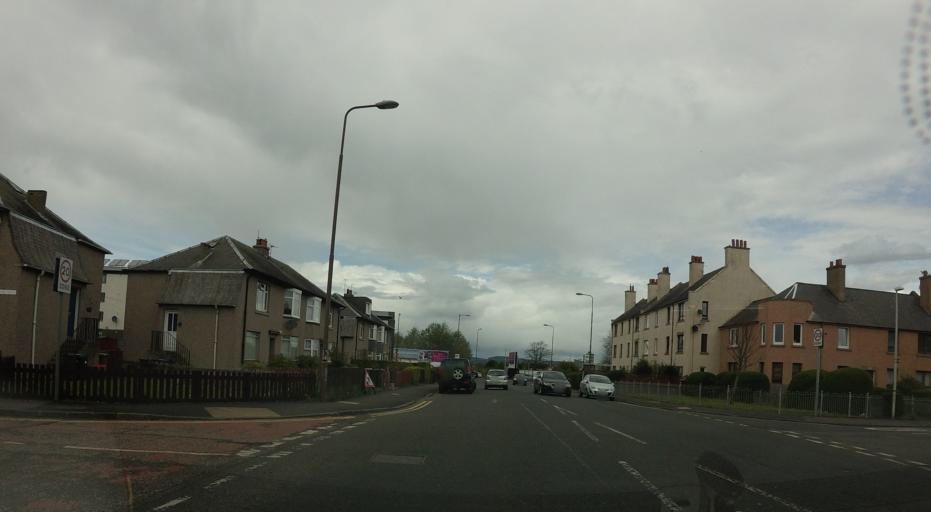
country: GB
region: Scotland
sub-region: Edinburgh
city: Edinburgh
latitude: 55.9763
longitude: -3.2391
